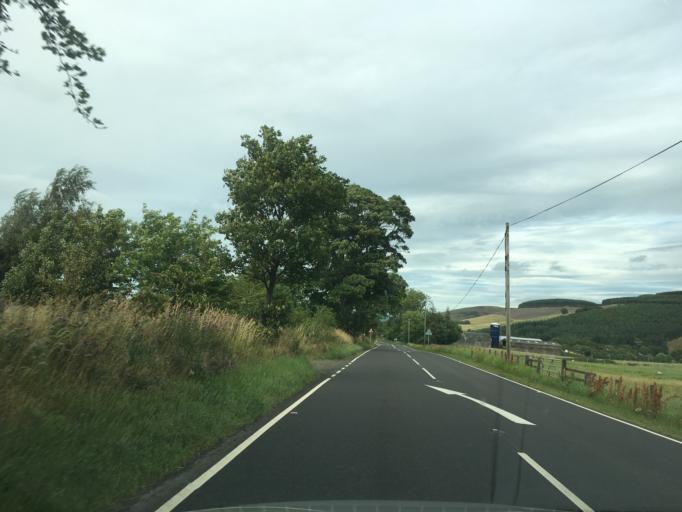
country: GB
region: Scotland
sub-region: South Lanarkshire
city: Biggar
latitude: 55.5844
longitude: -3.5618
